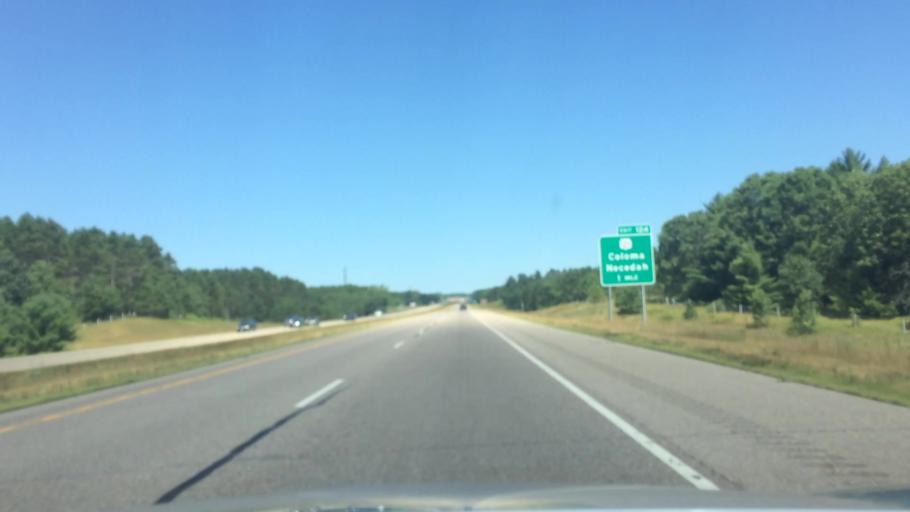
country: US
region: Wisconsin
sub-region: Marquette County
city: Westfield
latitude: 44.0183
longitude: -89.5130
